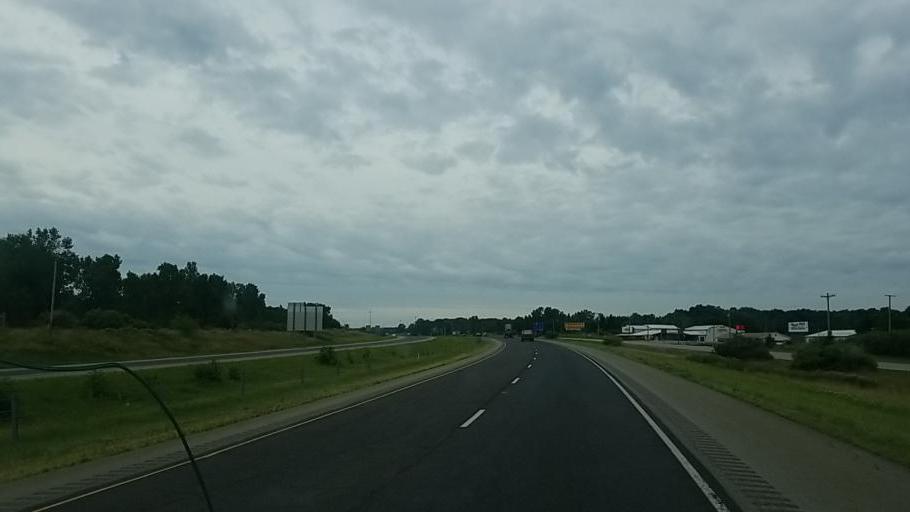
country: US
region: Indiana
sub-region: Steuben County
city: Fremont
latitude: 41.7161
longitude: -85.0036
